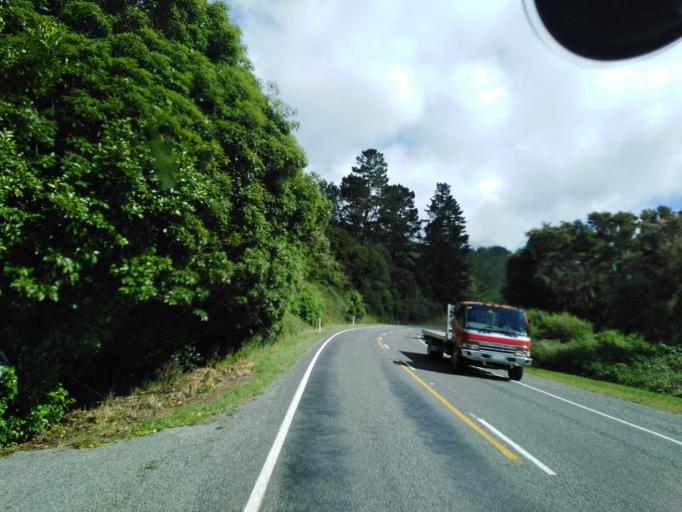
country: NZ
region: Nelson
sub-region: Nelson City
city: Nelson
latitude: -41.2909
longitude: 173.5723
